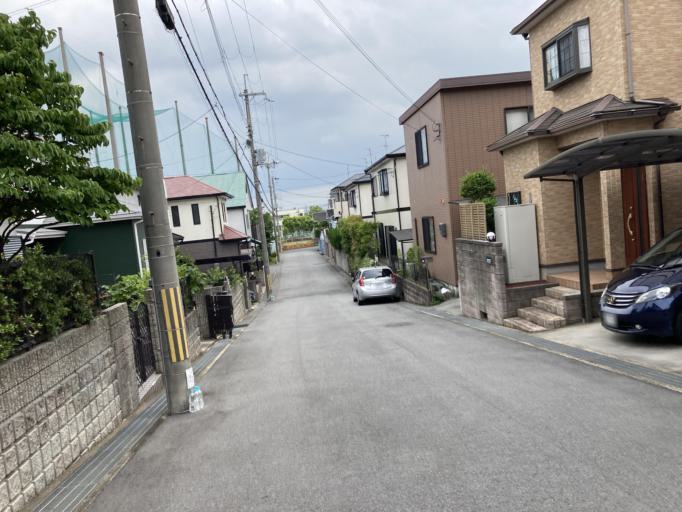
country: JP
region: Nara
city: Tawaramoto
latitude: 34.5644
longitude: 135.7143
